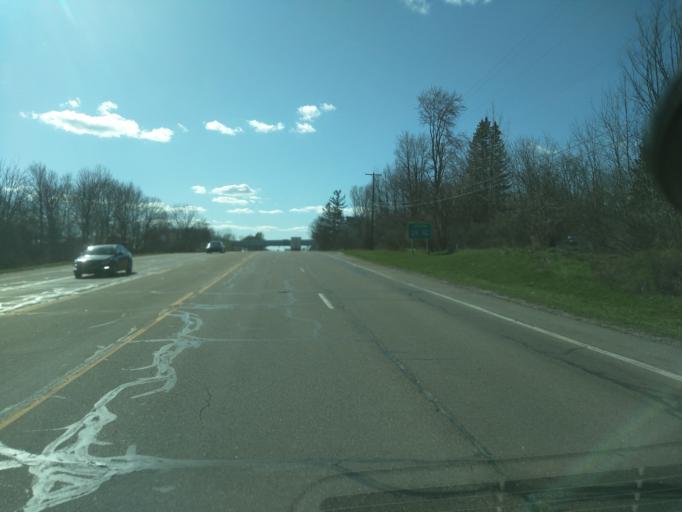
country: US
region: Michigan
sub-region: Eaton County
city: Waverly
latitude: 42.7832
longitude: -84.6607
